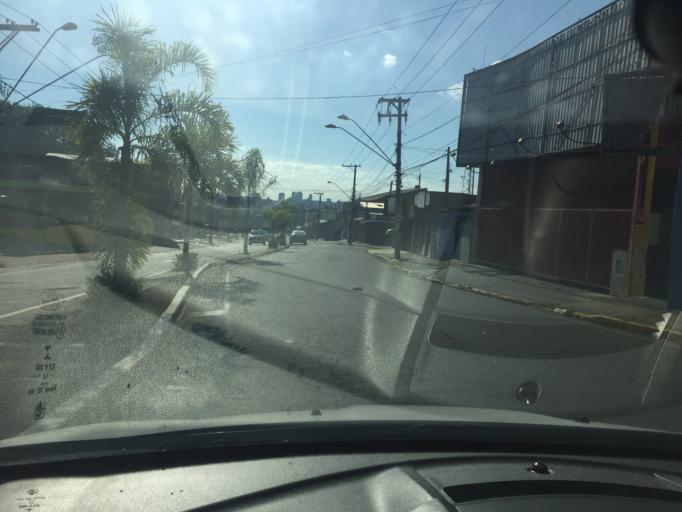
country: BR
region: Sao Paulo
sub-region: Varzea Paulista
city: Varzea Paulista
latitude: -23.2082
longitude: -46.8494
